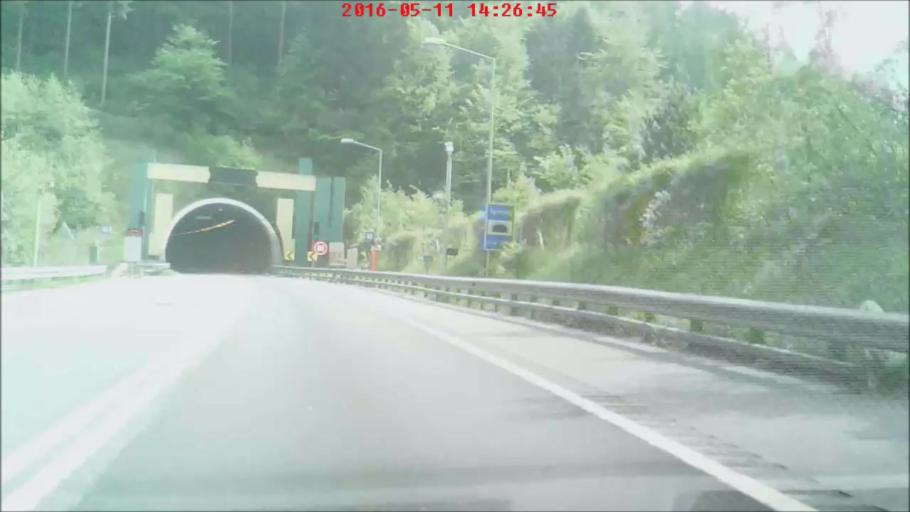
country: AT
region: Upper Austria
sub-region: Politischer Bezirk Kirchdorf an der Krems
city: Micheldorf in Oberoesterreich
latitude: 47.8134
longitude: 14.1697
